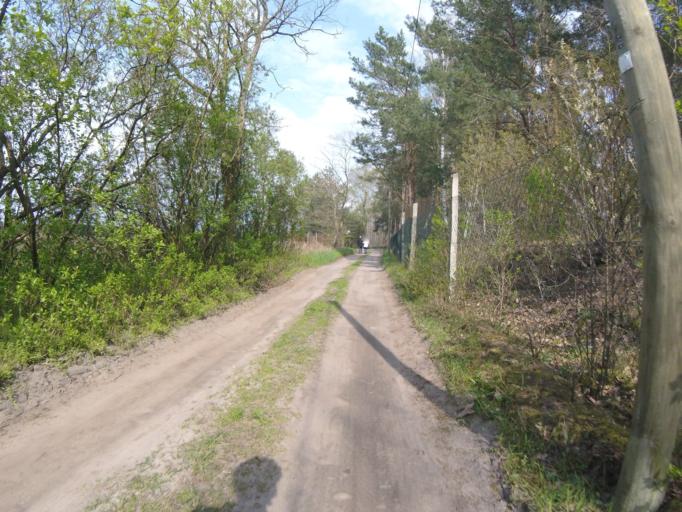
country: DE
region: Brandenburg
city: Bestensee
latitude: 52.2320
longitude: 13.6097
